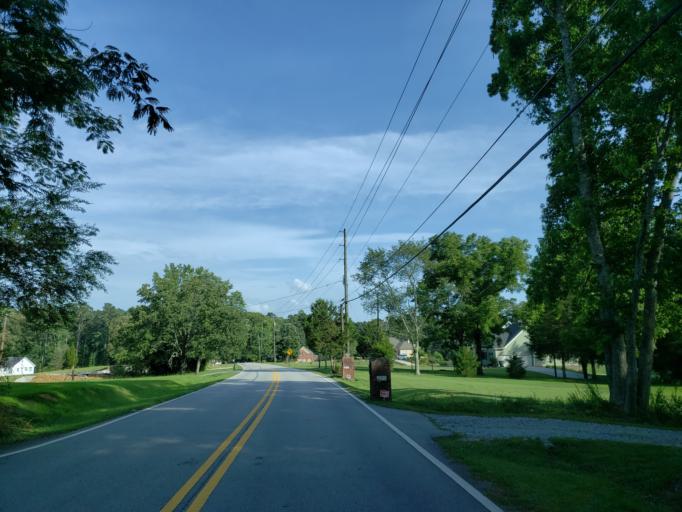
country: US
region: Georgia
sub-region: Paulding County
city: Hiram
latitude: 33.9142
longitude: -84.7172
